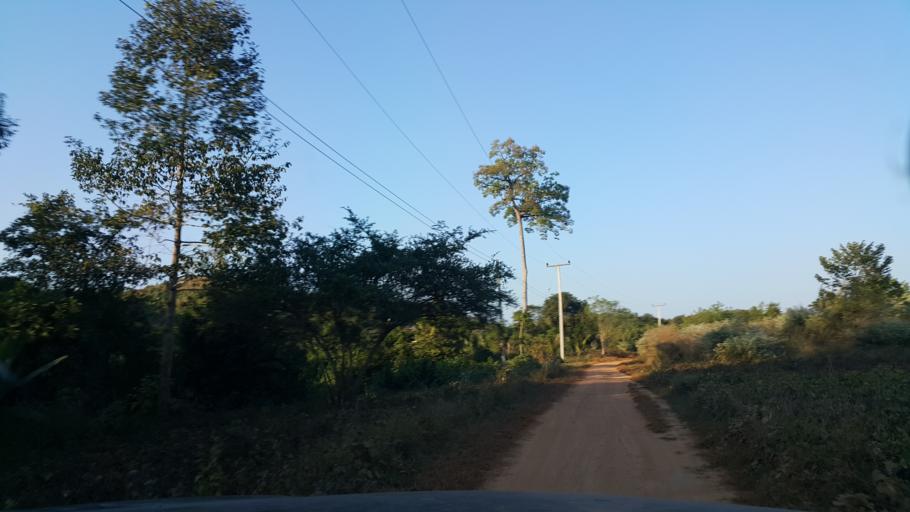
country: TH
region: Sukhothai
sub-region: Amphoe Si Satchanalai
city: Si Satchanalai
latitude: 17.5890
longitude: 99.6148
